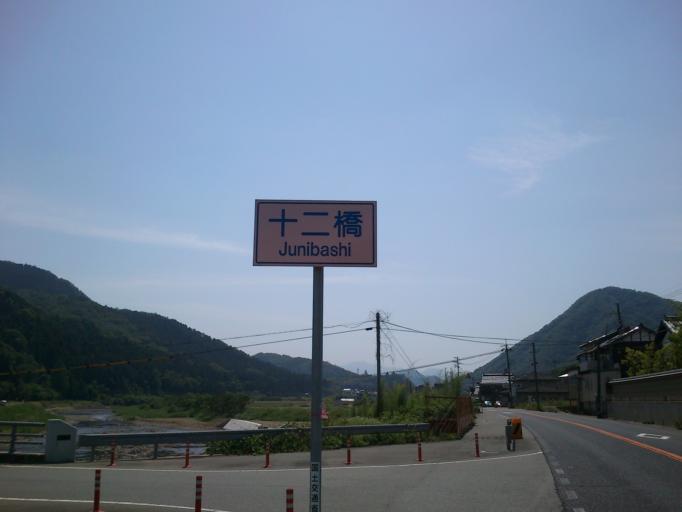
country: JP
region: Kyoto
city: Fukuchiyama
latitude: 35.3337
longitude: 135.0841
